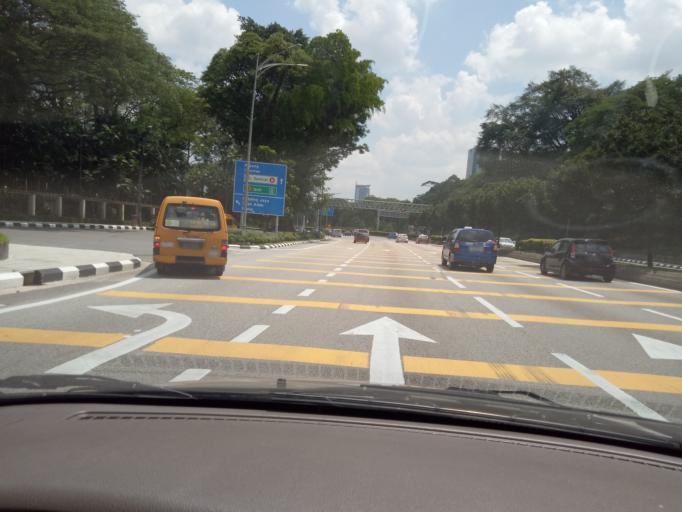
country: MY
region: Kuala Lumpur
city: Kuala Lumpur
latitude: 3.1336
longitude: 101.6975
